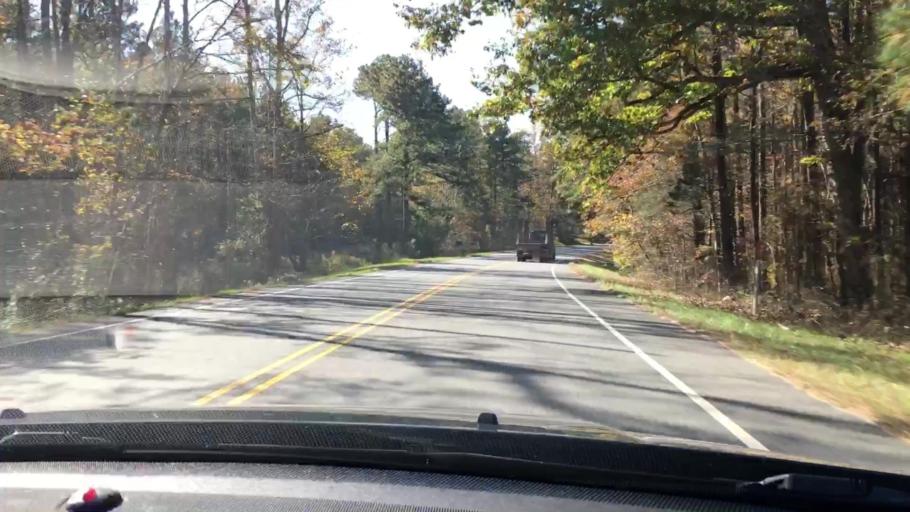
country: US
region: Virginia
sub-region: King William County
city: Central Garage
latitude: 37.7903
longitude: -77.2165
